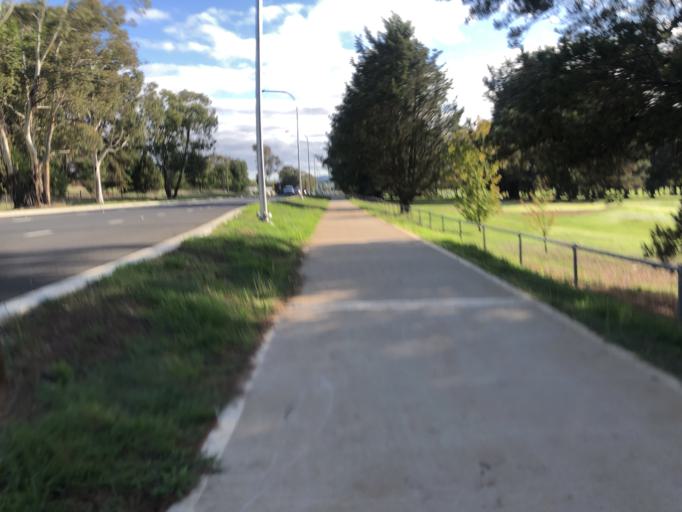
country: AU
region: New South Wales
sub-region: Orange Municipality
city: Orange
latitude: -33.3114
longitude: 149.0952
